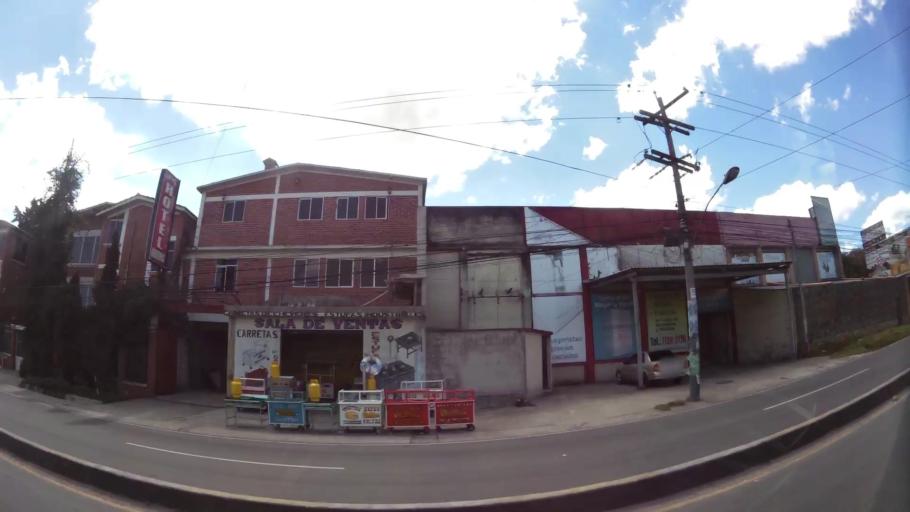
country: GT
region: Quetzaltenango
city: Quetzaltenango
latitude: 14.8563
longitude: -91.5376
